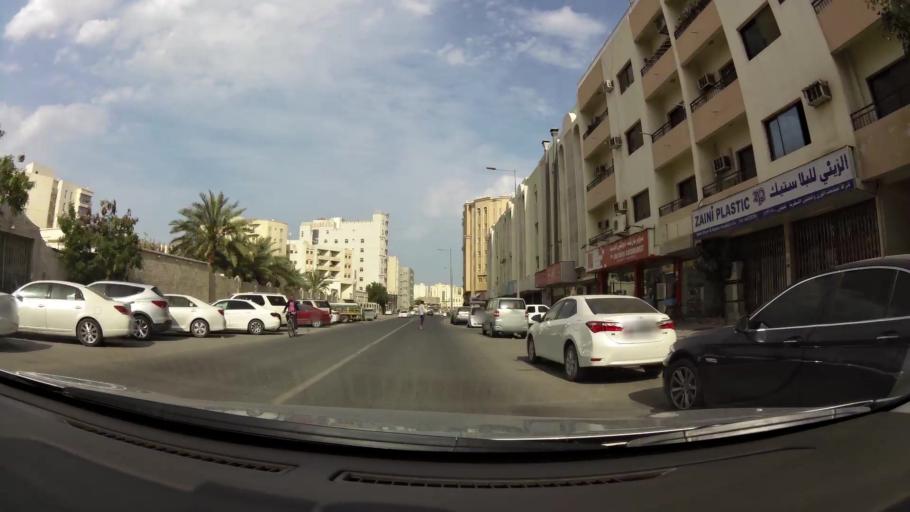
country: QA
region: Baladiyat ad Dawhah
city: Doha
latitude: 25.2803
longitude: 51.5119
